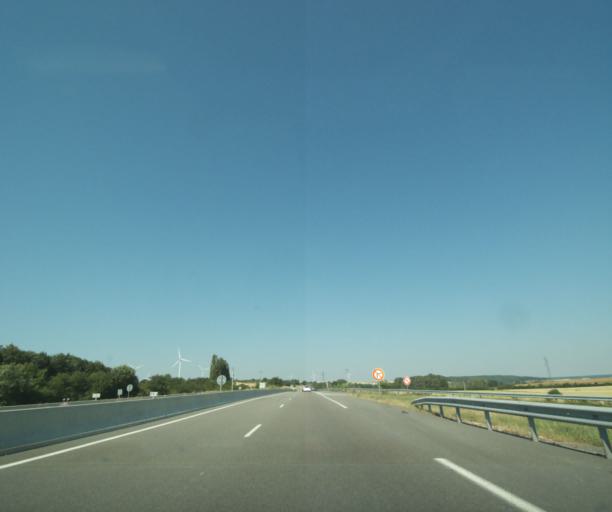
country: FR
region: Lorraine
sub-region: Departement de la Meuse
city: Lerouville
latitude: 48.7055
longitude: 5.4640
